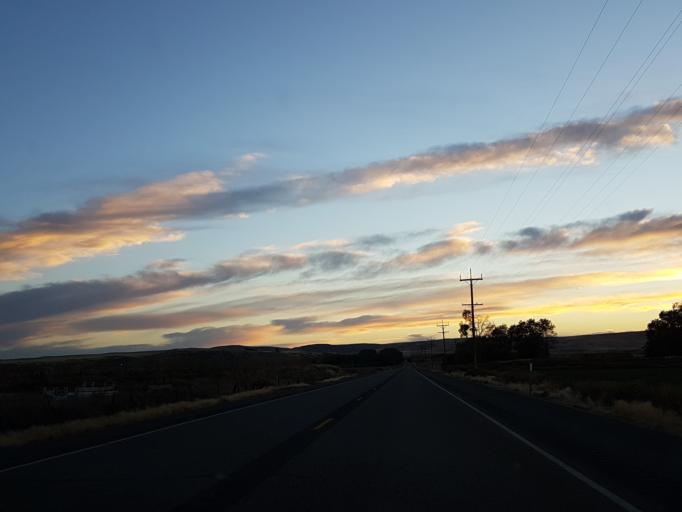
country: US
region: Oregon
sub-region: Malheur County
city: Vale
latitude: 43.9336
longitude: -117.3841
